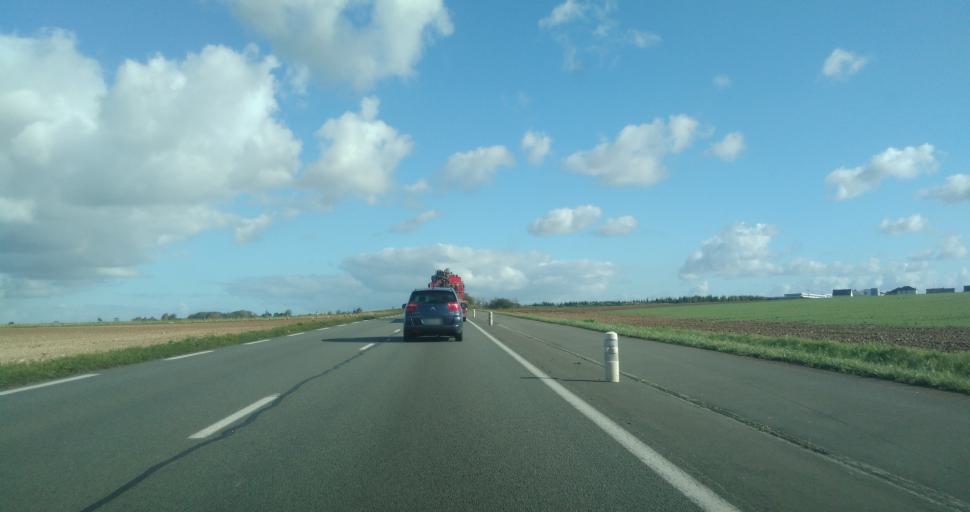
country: FR
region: Nord-Pas-de-Calais
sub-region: Departement du Pas-de-Calais
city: Anzin-Saint-Aubin
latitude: 50.3234
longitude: 2.7380
